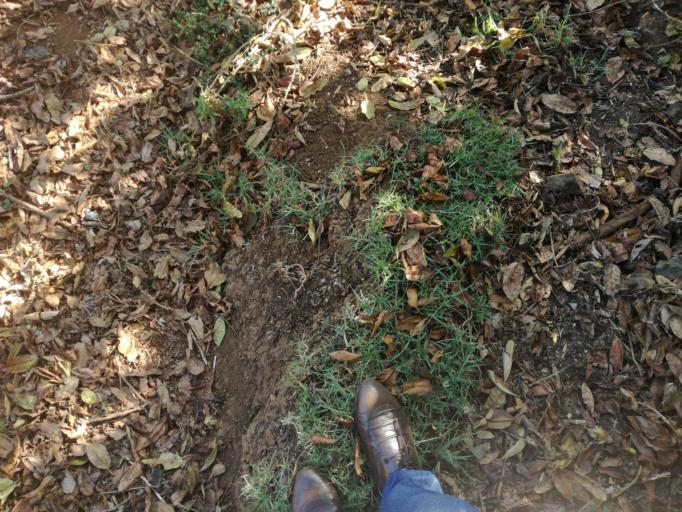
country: KE
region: Kirinyaga
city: Keruguya
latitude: -0.3866
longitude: 37.1397
